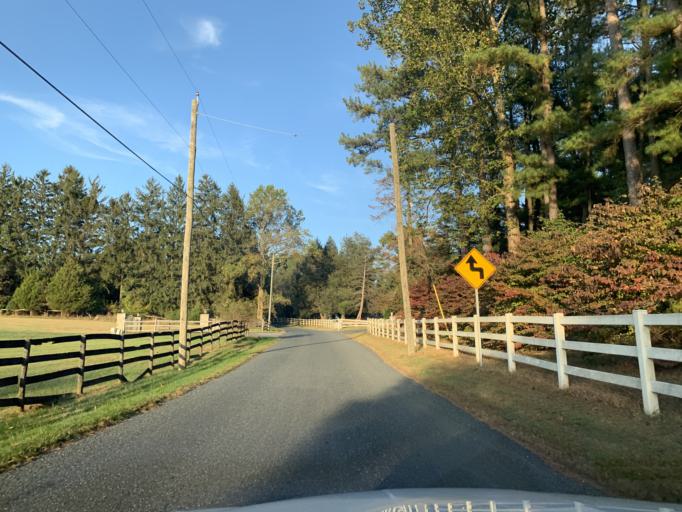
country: US
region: Maryland
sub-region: Harford County
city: Fallston
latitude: 39.5108
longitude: -76.4235
